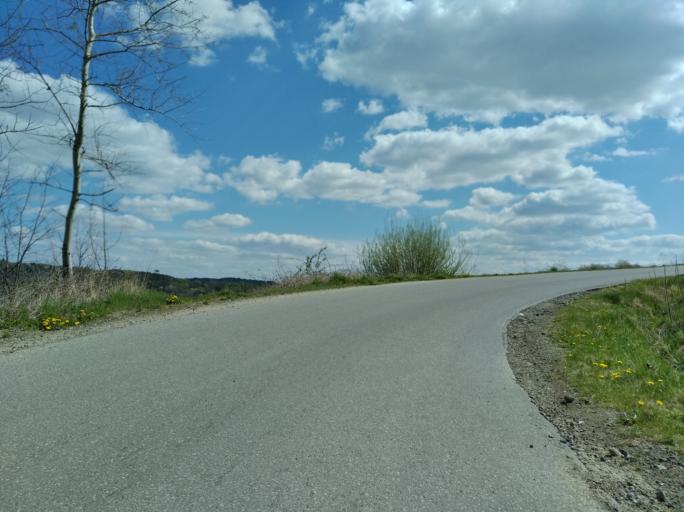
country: PL
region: Subcarpathian Voivodeship
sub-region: Powiat brzozowski
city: Wesola
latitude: 49.7738
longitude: 22.1321
